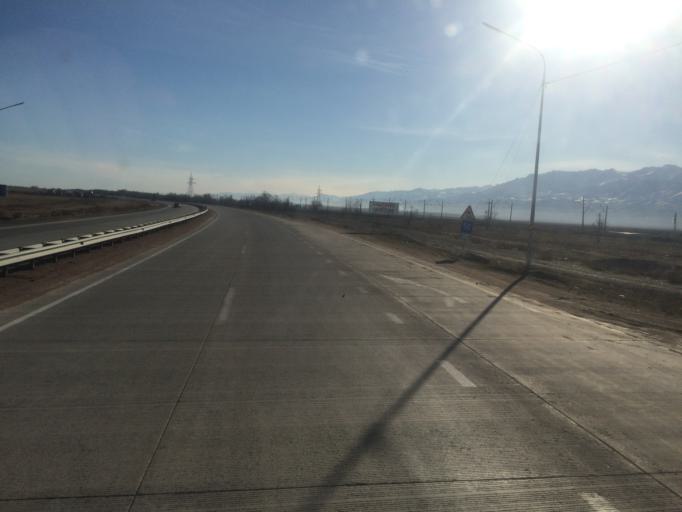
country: KG
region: Talas
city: Ivanovo-Alekseyevka
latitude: 42.9901
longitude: 72.1165
